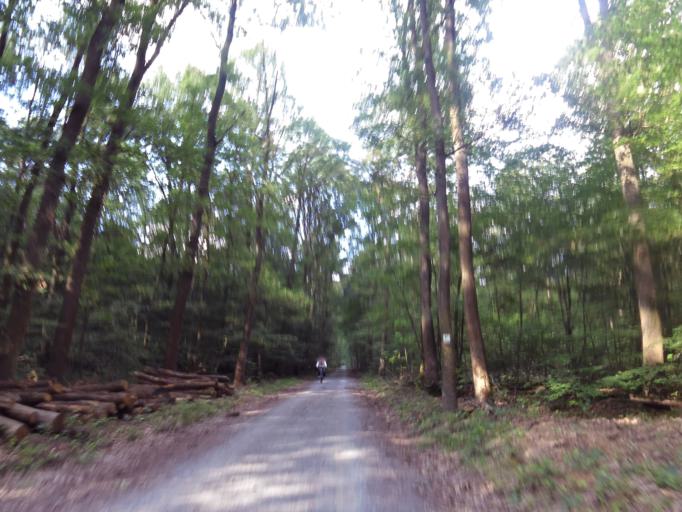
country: DE
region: Hesse
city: Niederrad
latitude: 50.0410
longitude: 8.6229
